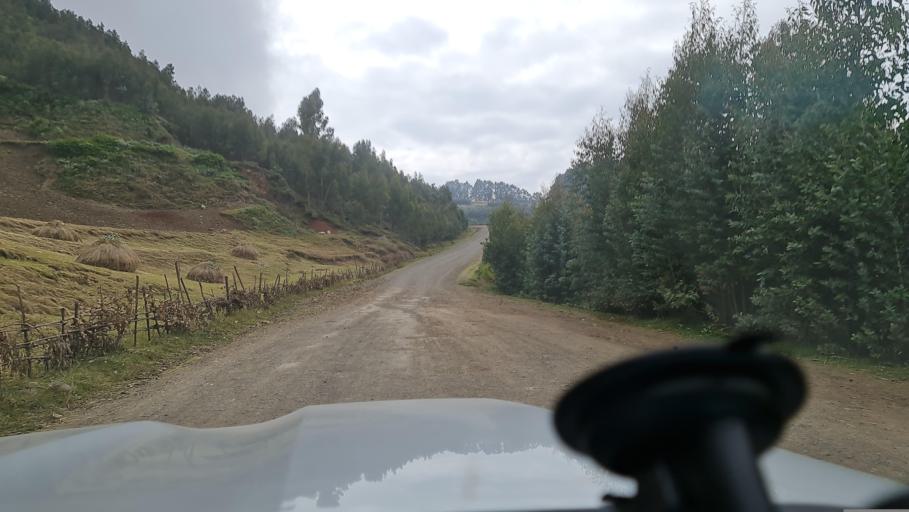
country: ET
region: Amhara
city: Abomsa
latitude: 10.1374
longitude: 39.7891
